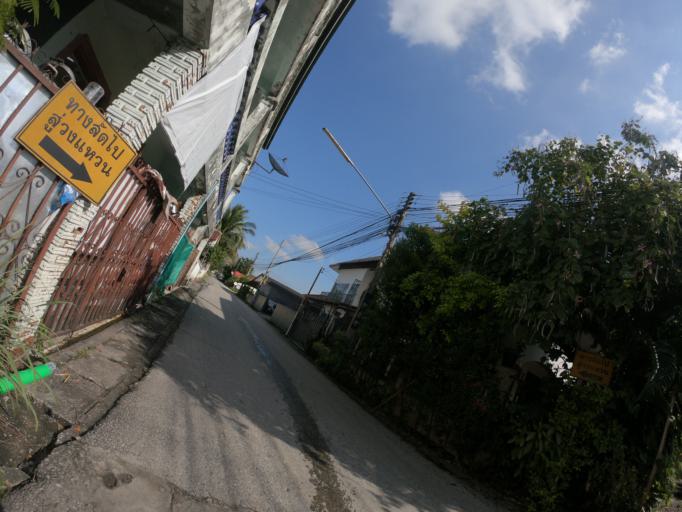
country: TH
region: Chiang Mai
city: Chiang Mai
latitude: 18.7855
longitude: 99.0391
